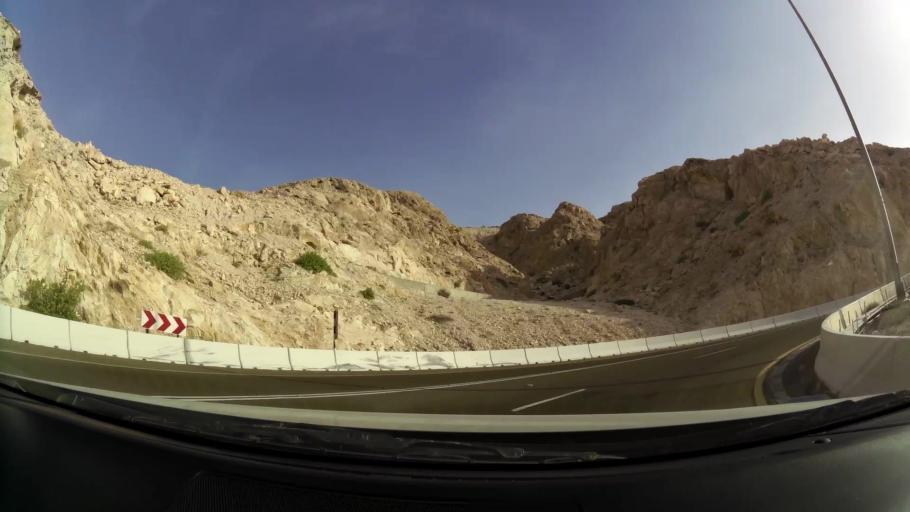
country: AE
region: Abu Dhabi
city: Al Ain
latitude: 24.0857
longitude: 55.7664
